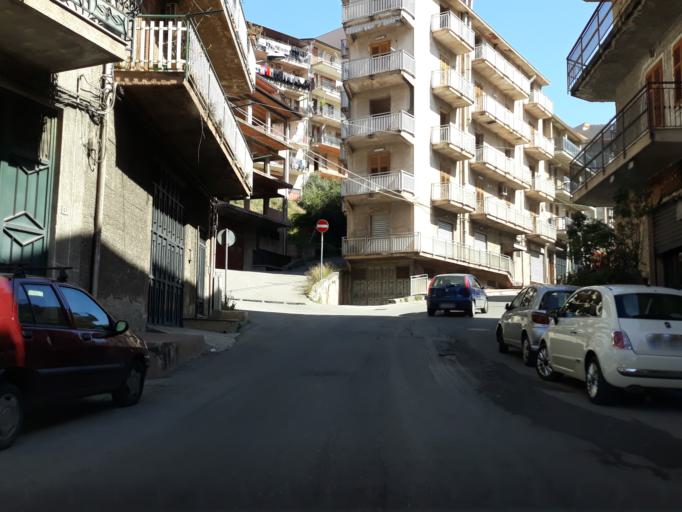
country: IT
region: Sicily
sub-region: Palermo
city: Belmonte Mezzagno
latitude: 38.0468
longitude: 13.3944
